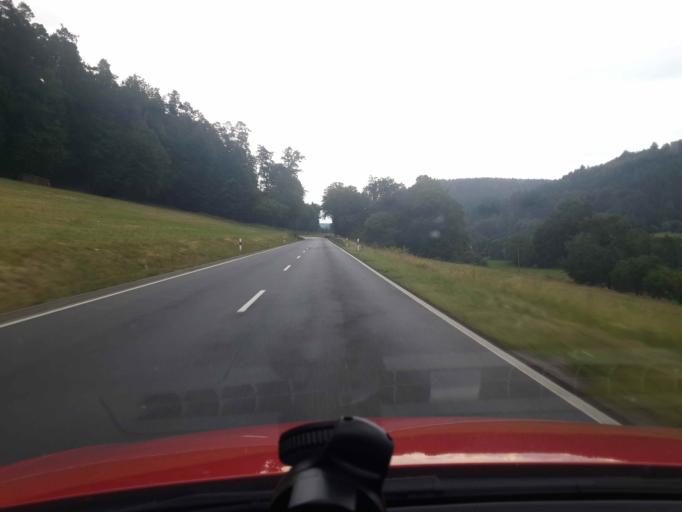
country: DE
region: Bavaria
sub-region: Regierungsbezirk Unterfranken
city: Kirchzell
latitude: 49.6068
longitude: 9.1999
